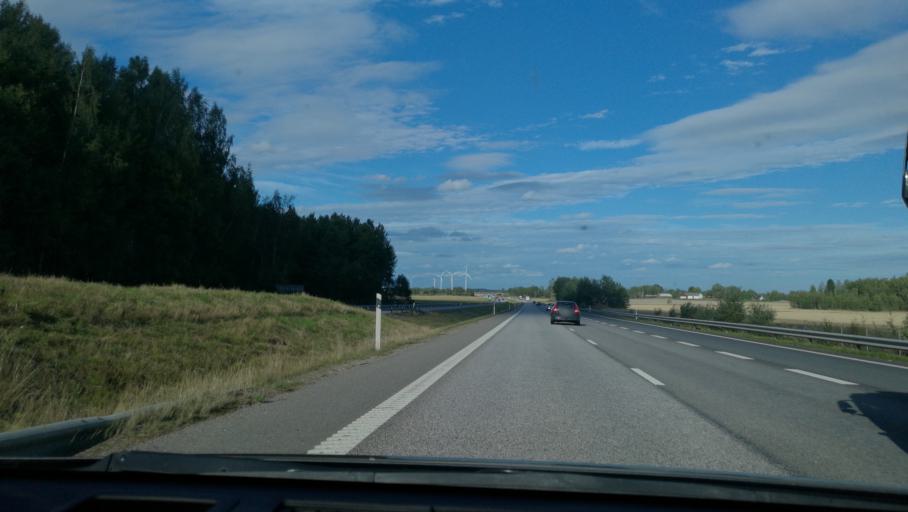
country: SE
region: OErebro
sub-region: Kumla Kommun
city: Kumla
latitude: 59.1418
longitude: 15.0870
